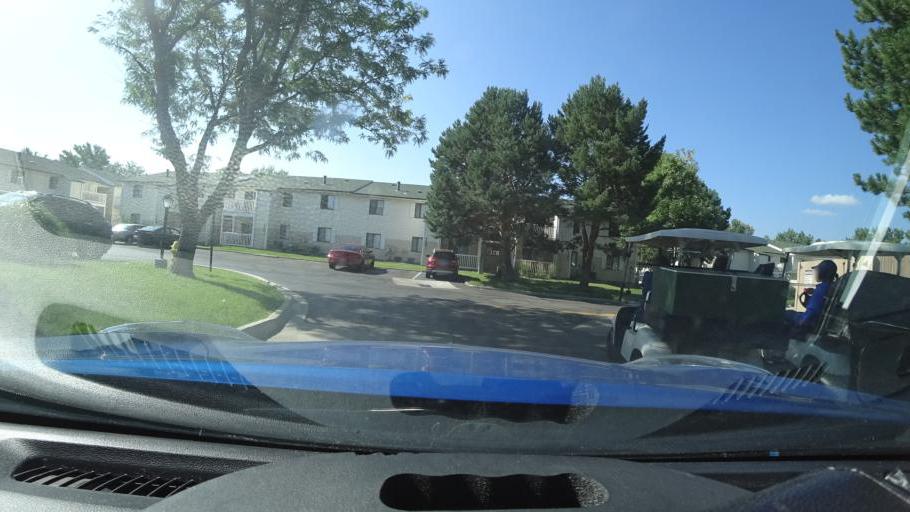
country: US
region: Colorado
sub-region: Adams County
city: Aurora
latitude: 39.7243
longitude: -104.8146
